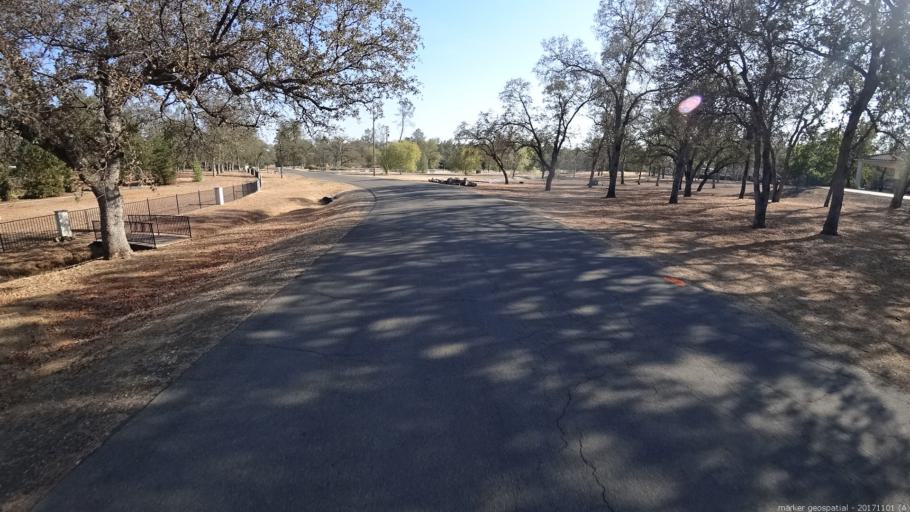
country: US
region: California
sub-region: Shasta County
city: Shasta Lake
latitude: 40.6783
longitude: -122.3348
